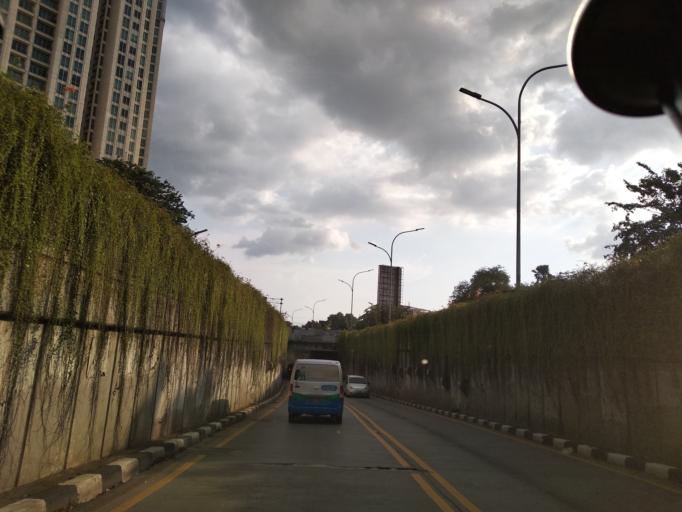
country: ID
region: Jakarta Raya
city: Jakarta
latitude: -6.2352
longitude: 106.7851
